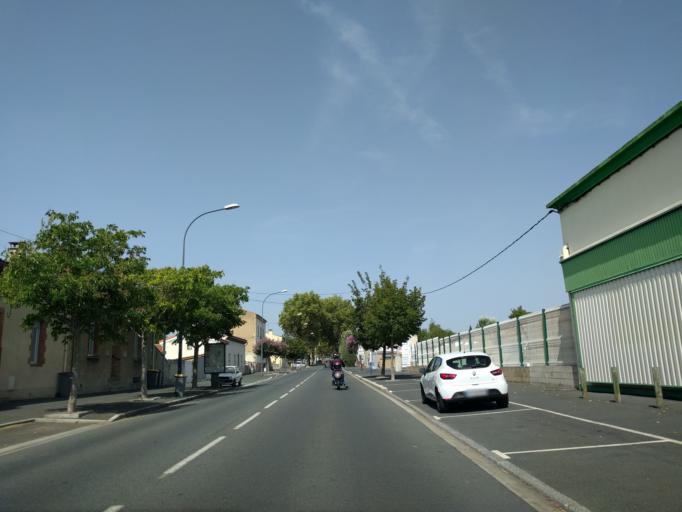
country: FR
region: Midi-Pyrenees
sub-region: Departement du Tarn
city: Castres
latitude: 43.6129
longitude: 2.2340
